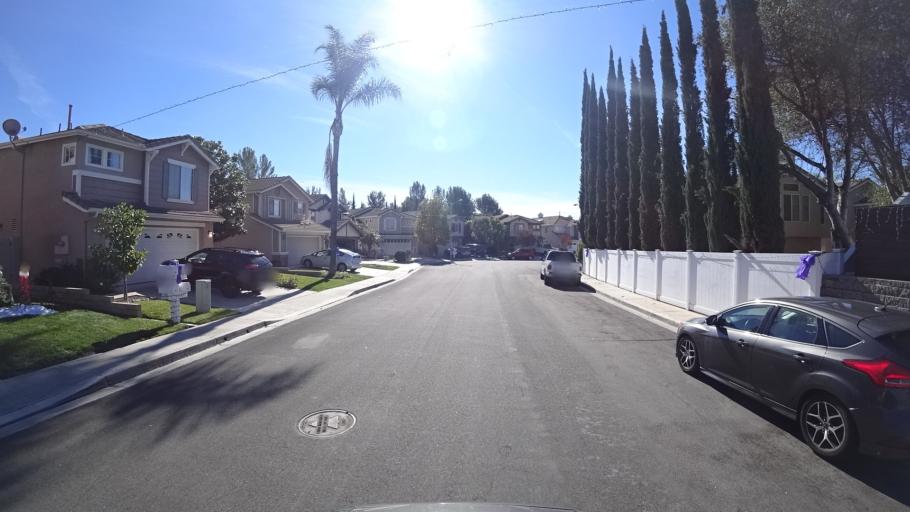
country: US
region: California
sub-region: Orange County
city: Coto De Caza
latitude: 33.5961
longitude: -117.5933
